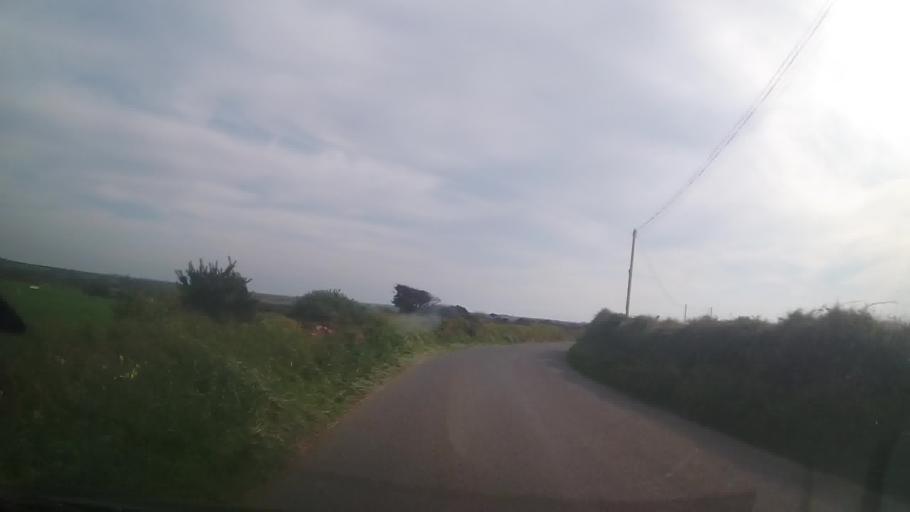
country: GB
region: Wales
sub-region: Pembrokeshire
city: Saint David's
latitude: 51.9094
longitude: -5.2407
